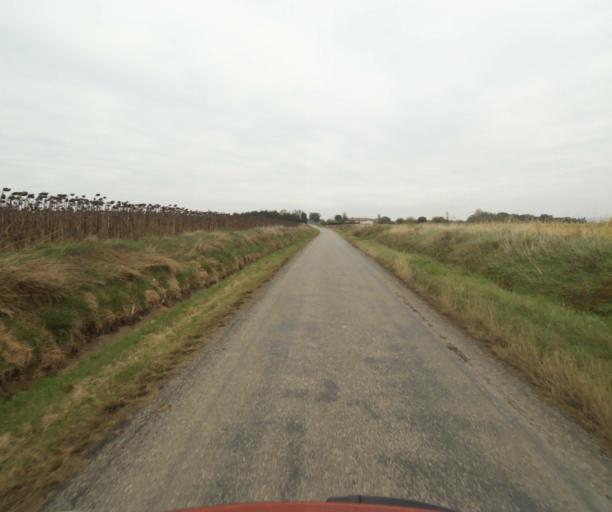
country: FR
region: Midi-Pyrenees
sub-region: Departement du Tarn-et-Garonne
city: Verdun-sur-Garonne
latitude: 43.8153
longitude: 1.1974
